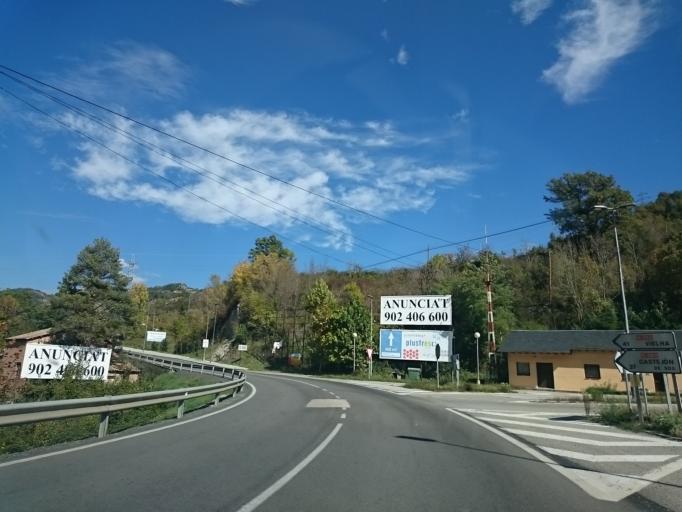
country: ES
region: Aragon
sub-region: Provincia de Huesca
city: Bonansa
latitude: 42.4011
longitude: 0.7421
